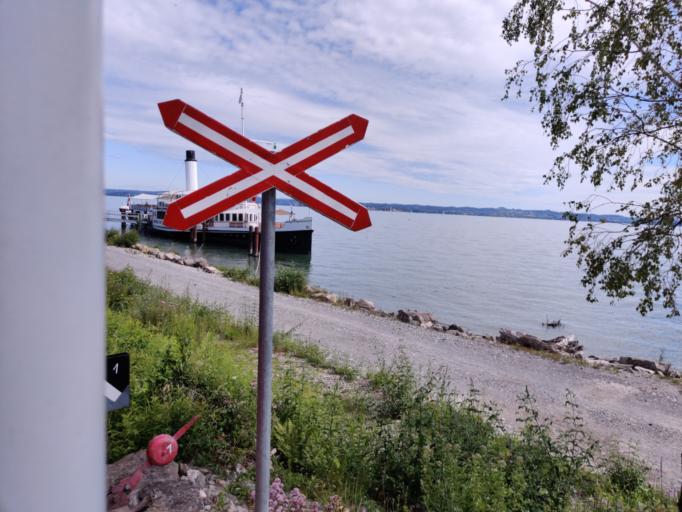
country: AT
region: Vorarlberg
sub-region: Politischer Bezirk Bregenz
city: Hard
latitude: 47.5056
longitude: 9.6699
